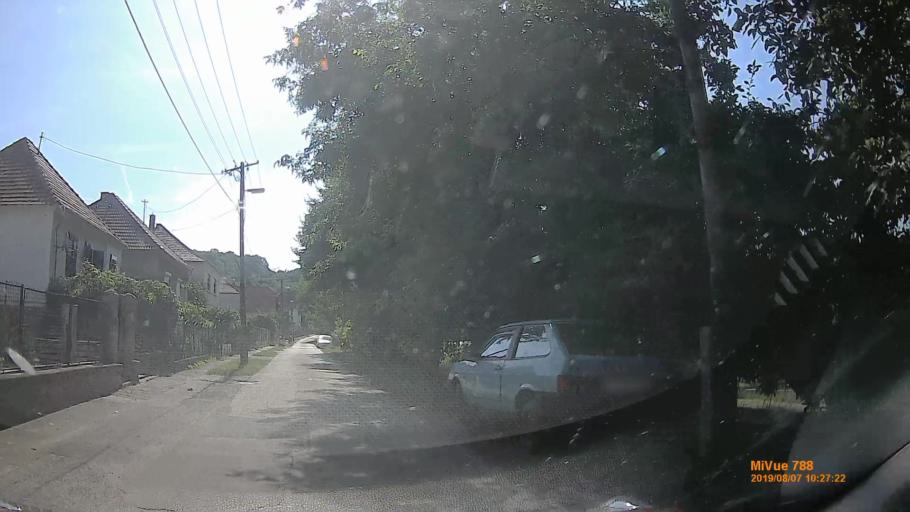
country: HU
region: Veszprem
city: Ajka
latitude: 47.0877
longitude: 17.5690
